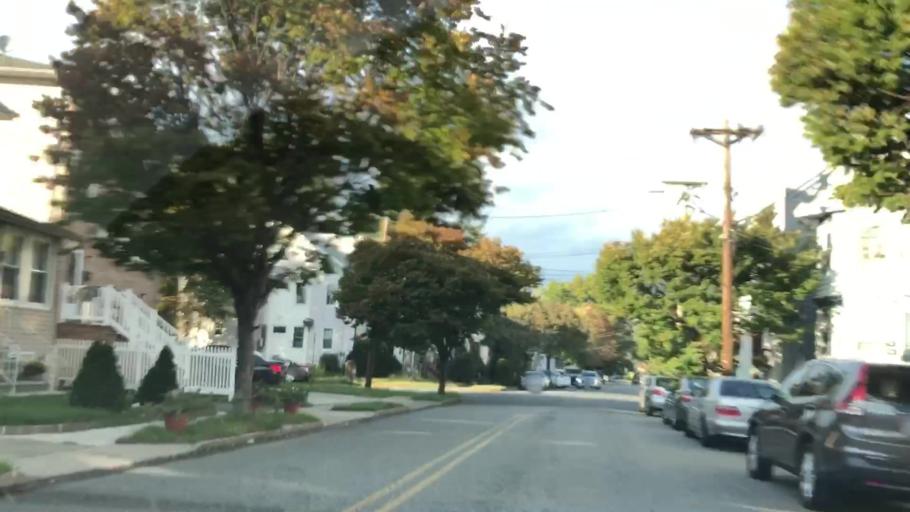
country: US
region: New Jersey
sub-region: Essex County
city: East Orange
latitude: 40.7839
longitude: -74.2045
